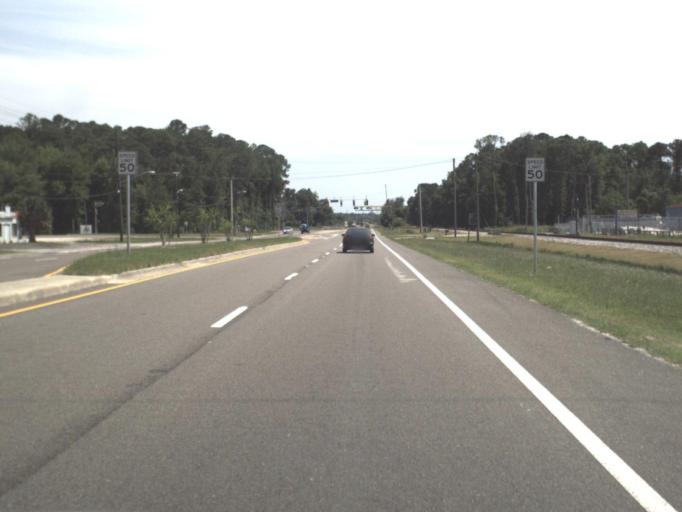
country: US
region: Florida
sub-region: Duval County
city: Jacksonville
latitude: 30.4066
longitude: -81.6501
